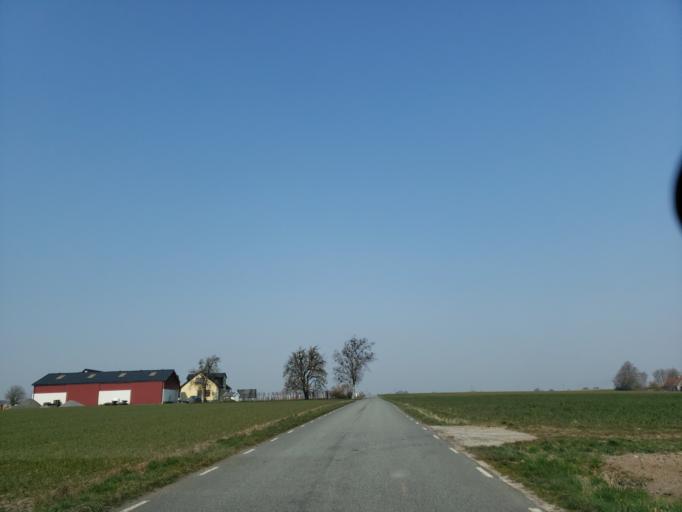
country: SE
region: Skane
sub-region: Simrishamns Kommun
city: Simrishamn
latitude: 55.4568
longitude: 14.2135
